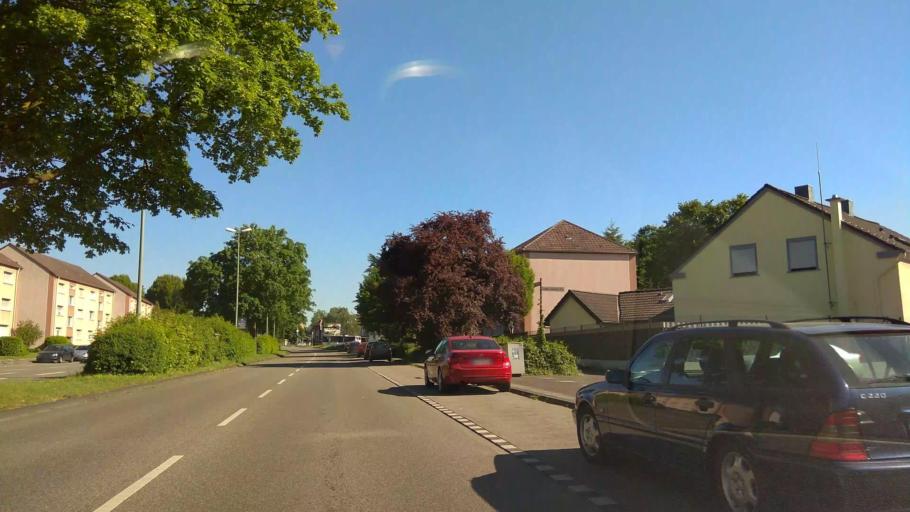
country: DE
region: North Rhine-Westphalia
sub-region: Regierungsbezirk Munster
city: Bottrop
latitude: 51.5134
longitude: 6.9346
